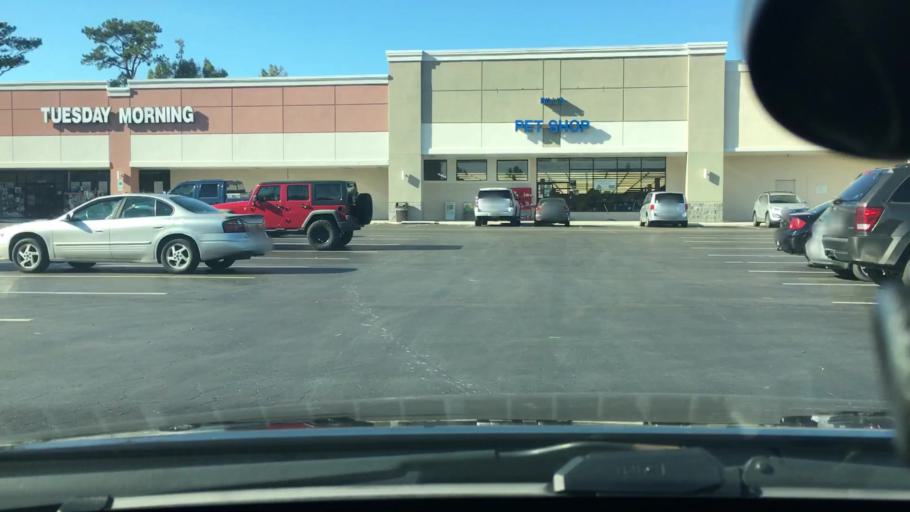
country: US
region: North Carolina
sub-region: Craven County
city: Trent Woods
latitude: 35.1057
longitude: -77.0841
